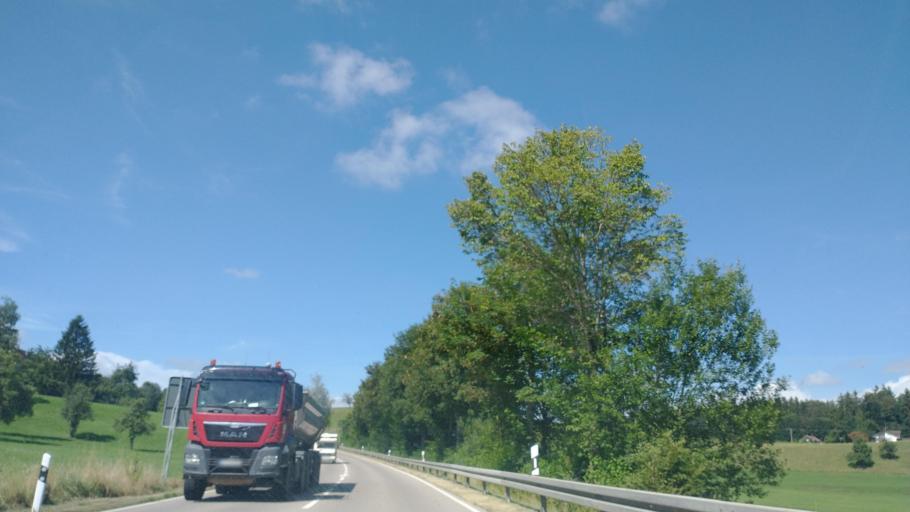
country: DE
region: Baden-Wuerttemberg
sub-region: Tuebingen Region
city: Neukirch
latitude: 47.6610
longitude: 9.7032
